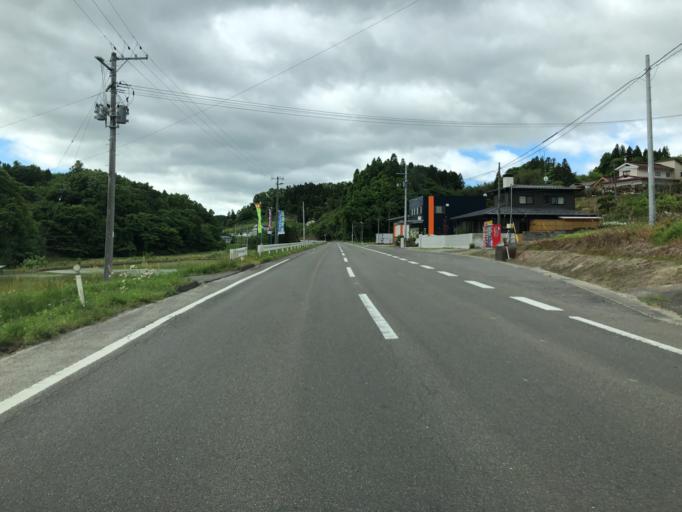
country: JP
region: Fukushima
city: Nihommatsu
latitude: 37.5509
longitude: 140.4597
